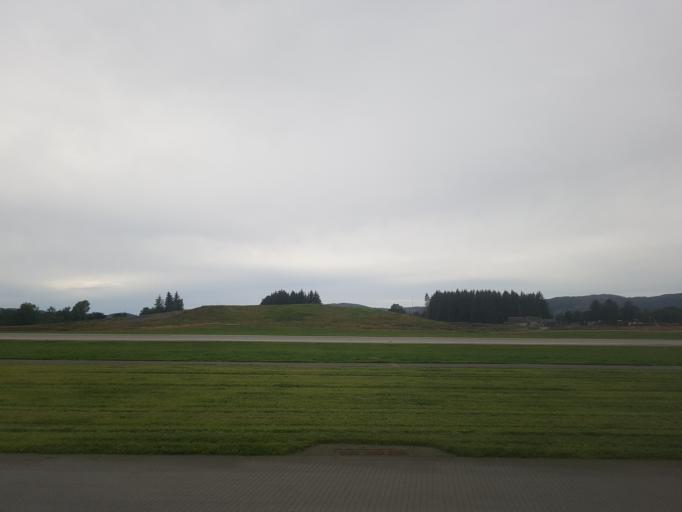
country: NO
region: Hordaland
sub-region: Bergen
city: Ytrebygda
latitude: 60.2928
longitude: 5.2216
